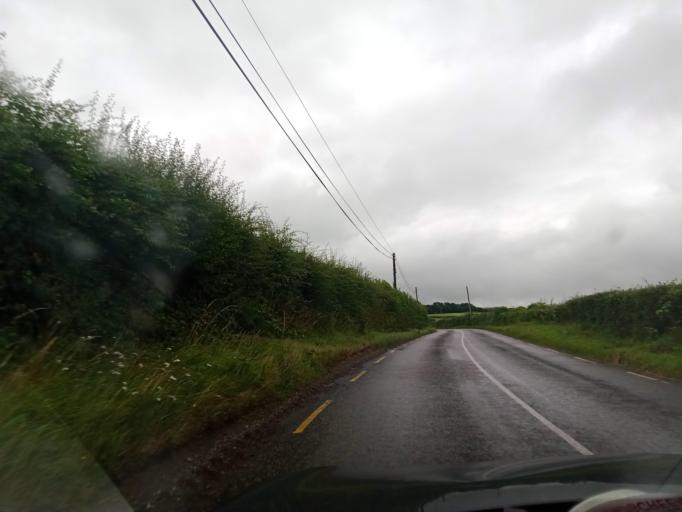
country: IE
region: Leinster
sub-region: Laois
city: Abbeyleix
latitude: 52.9108
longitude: -7.3156
